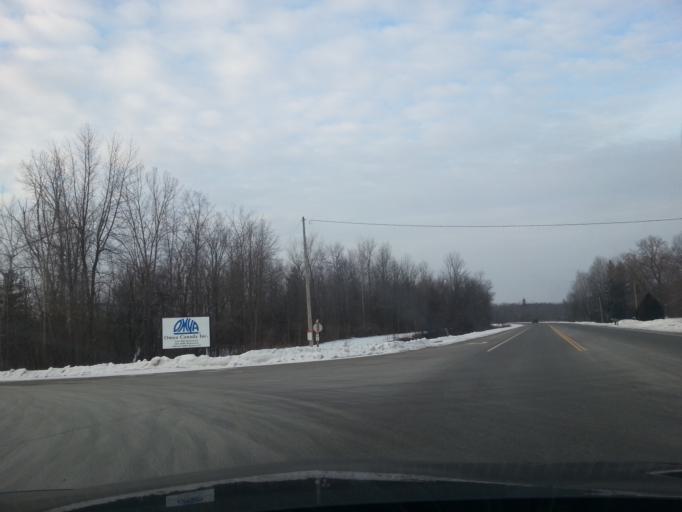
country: CA
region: Ontario
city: Perth
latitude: 44.8803
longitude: -76.3285
